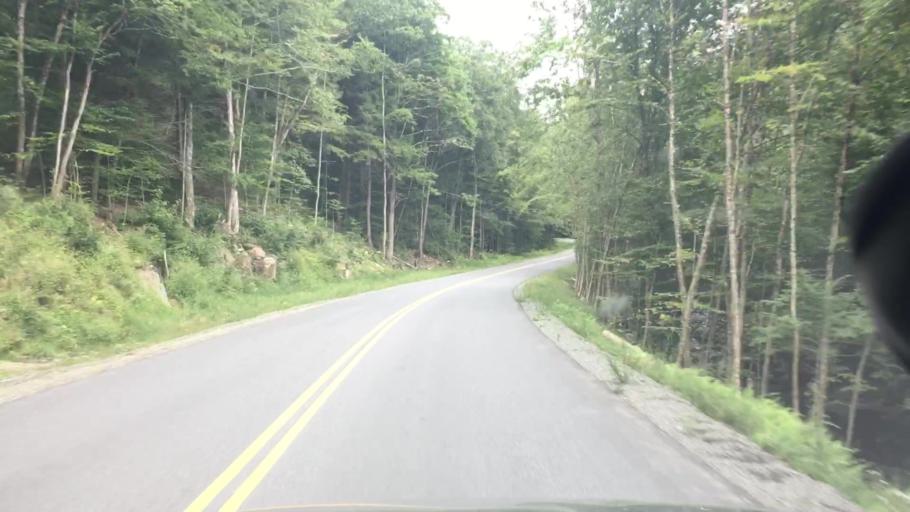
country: US
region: Massachusetts
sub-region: Franklin County
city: Colrain
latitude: 42.7708
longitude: -72.7661
